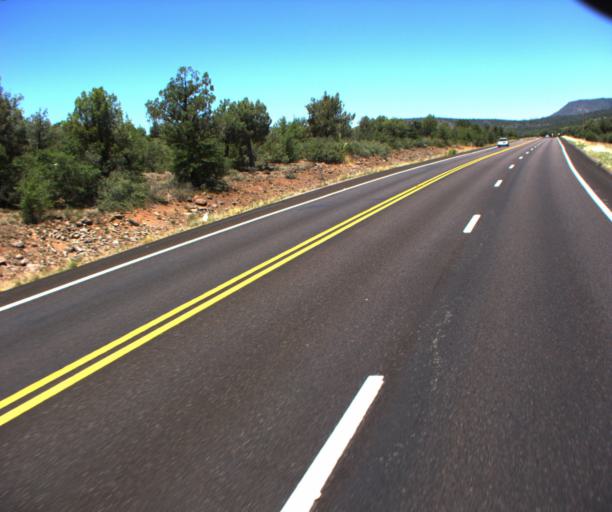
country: US
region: Arizona
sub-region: Gila County
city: Pine
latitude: 34.3242
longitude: -111.4174
